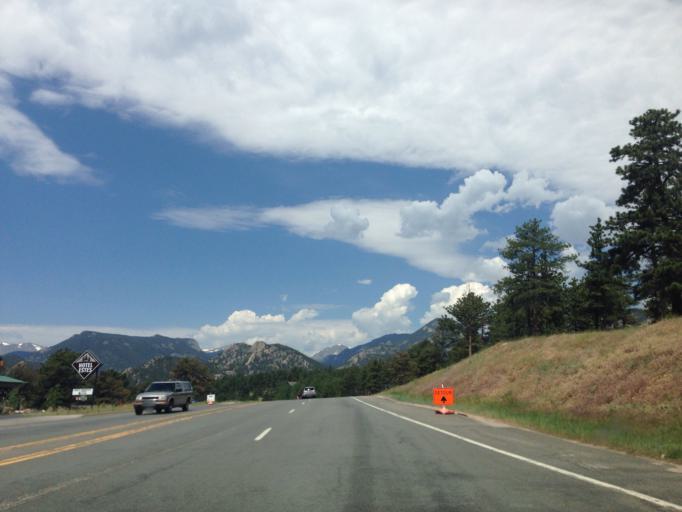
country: US
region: Colorado
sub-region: Larimer County
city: Estes Park
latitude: 40.3834
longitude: -105.5004
